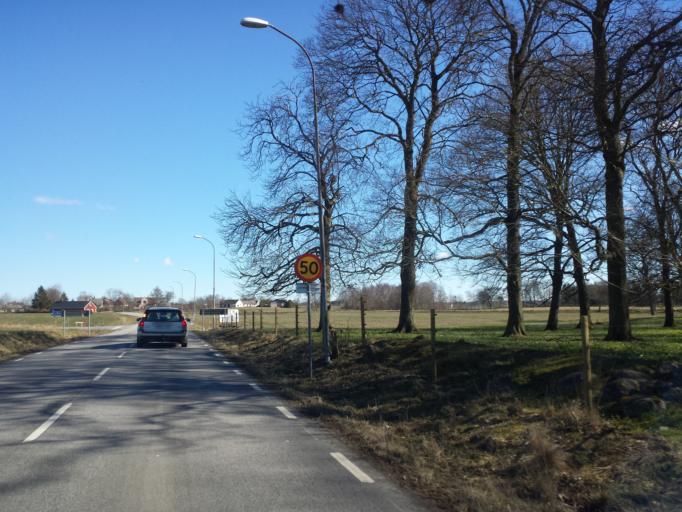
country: SE
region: Skane
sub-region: Tomelilla Kommun
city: Tomelilla
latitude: 55.6478
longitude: 13.8922
